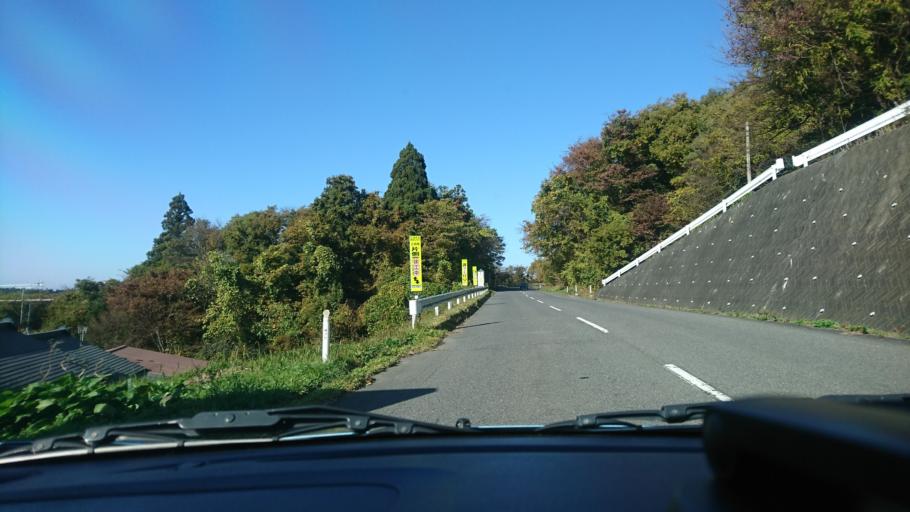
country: JP
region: Iwate
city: Ichinoseki
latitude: 38.7997
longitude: 141.2557
